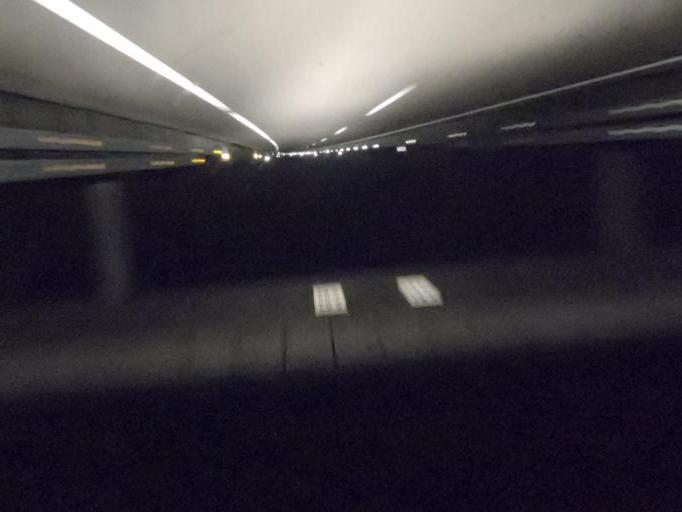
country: ES
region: Castille and Leon
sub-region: Provincia de Zamora
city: Vega de Tera
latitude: 42.0086
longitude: -6.1186
